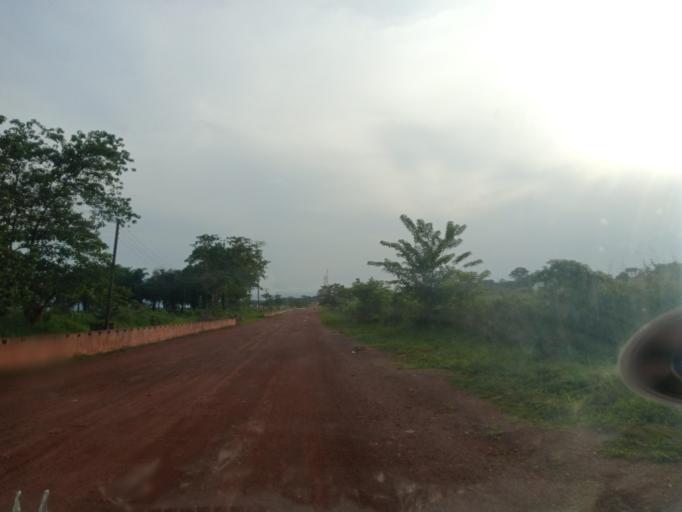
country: SL
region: Southern Province
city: Largo
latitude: 8.1154
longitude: -12.0608
